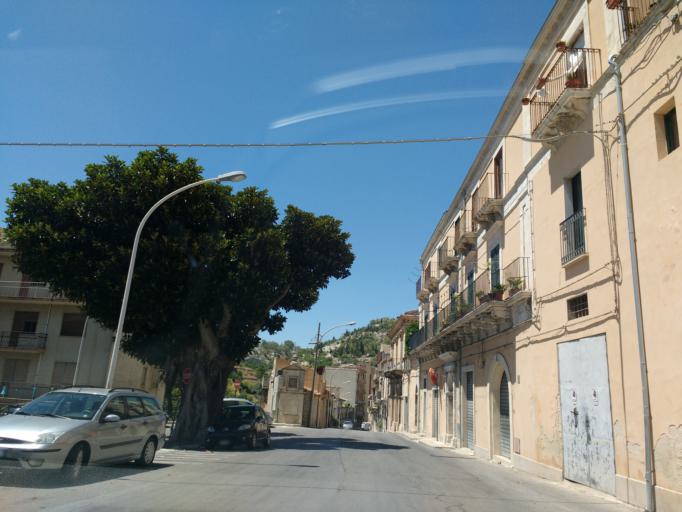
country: IT
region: Sicily
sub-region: Ragusa
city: Modica
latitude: 36.8656
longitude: 14.7589
